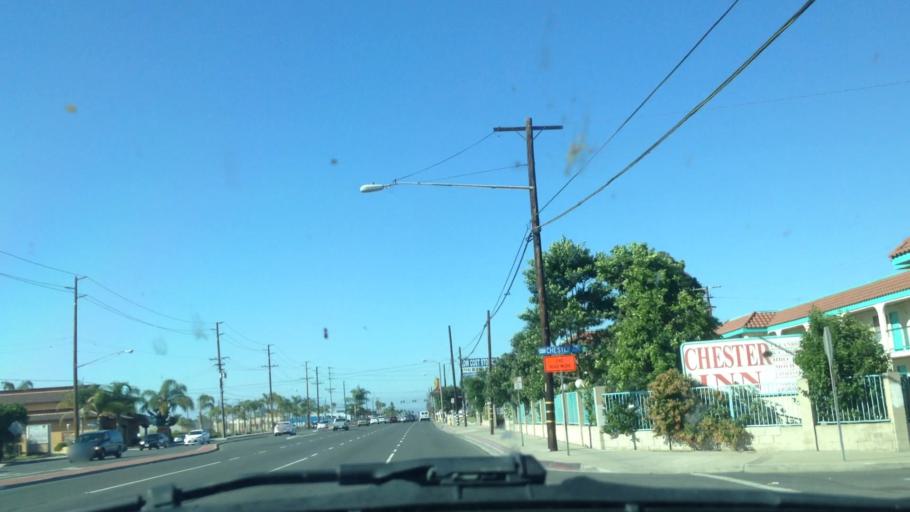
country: US
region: California
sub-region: Orange County
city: Stanton
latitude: 33.8037
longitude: -117.9930
